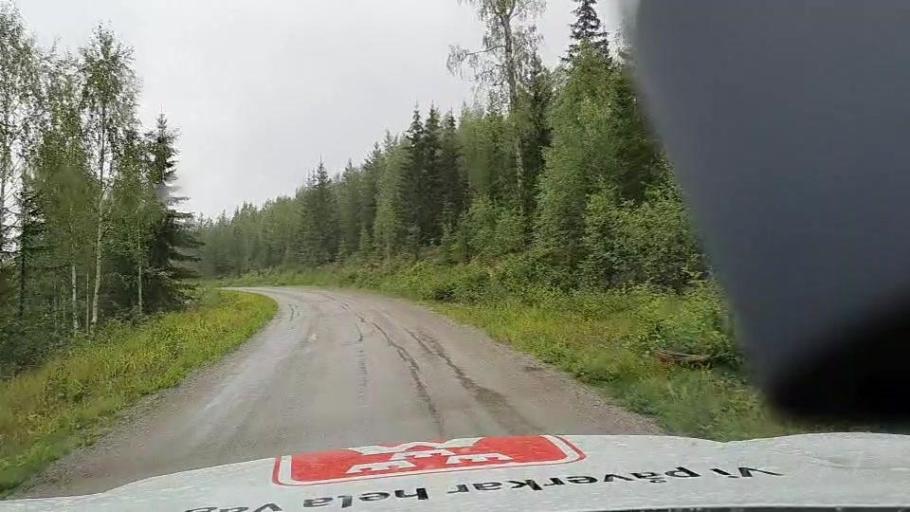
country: SE
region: Jaemtland
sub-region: OEstersunds Kommun
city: Brunflo
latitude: 62.8249
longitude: 15.0219
